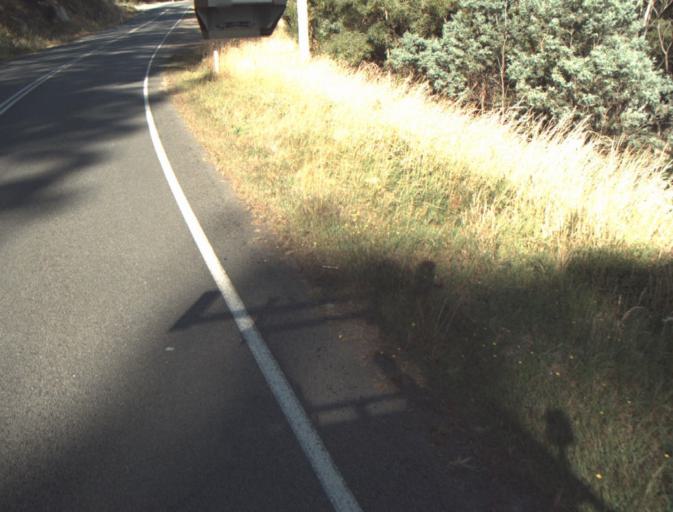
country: AU
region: Tasmania
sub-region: Launceston
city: Newstead
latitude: -41.4197
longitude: 147.2755
